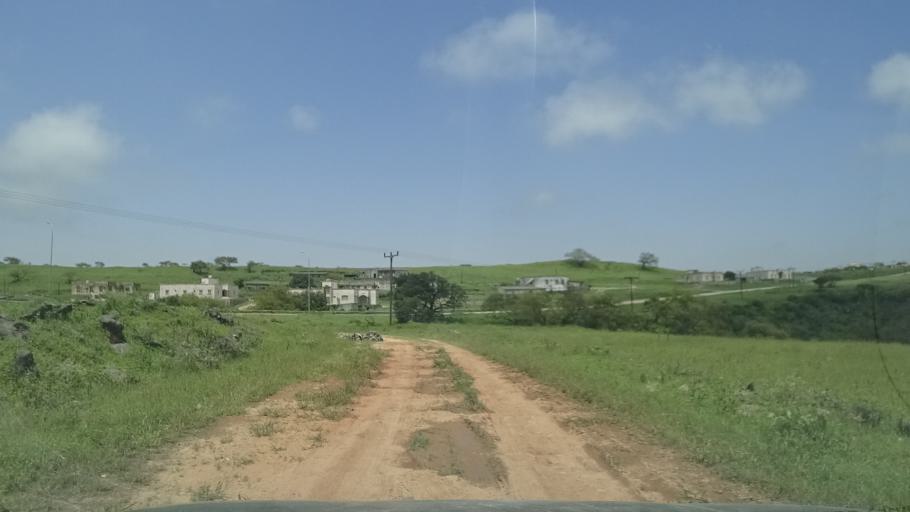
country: OM
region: Zufar
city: Salalah
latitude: 17.2197
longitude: 54.2573
